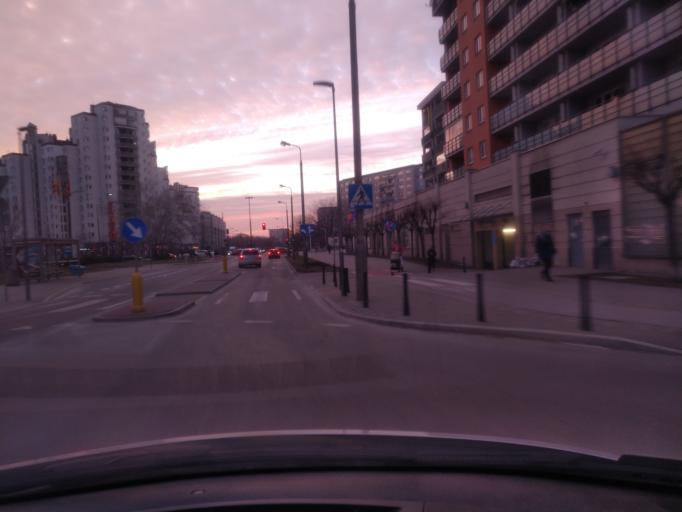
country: PL
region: Masovian Voivodeship
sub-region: Warszawa
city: Praga Poludnie
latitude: 52.2217
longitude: 21.0928
